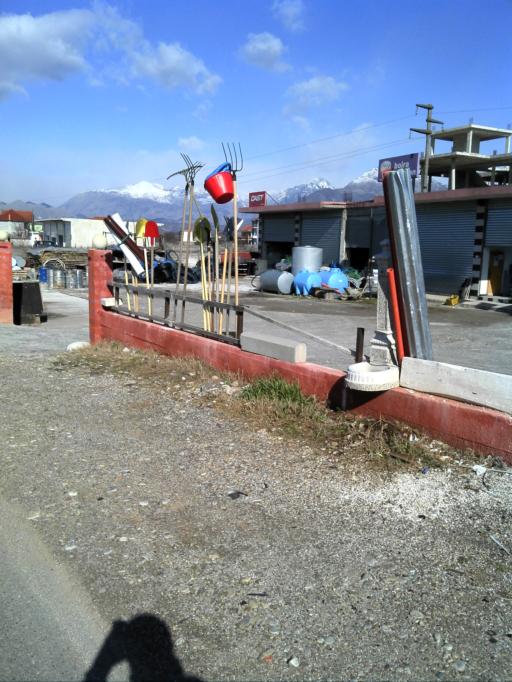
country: AL
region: Shkoder
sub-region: Rrethi i Shkodres
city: Shkoder
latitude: 42.0983
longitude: 19.5059
